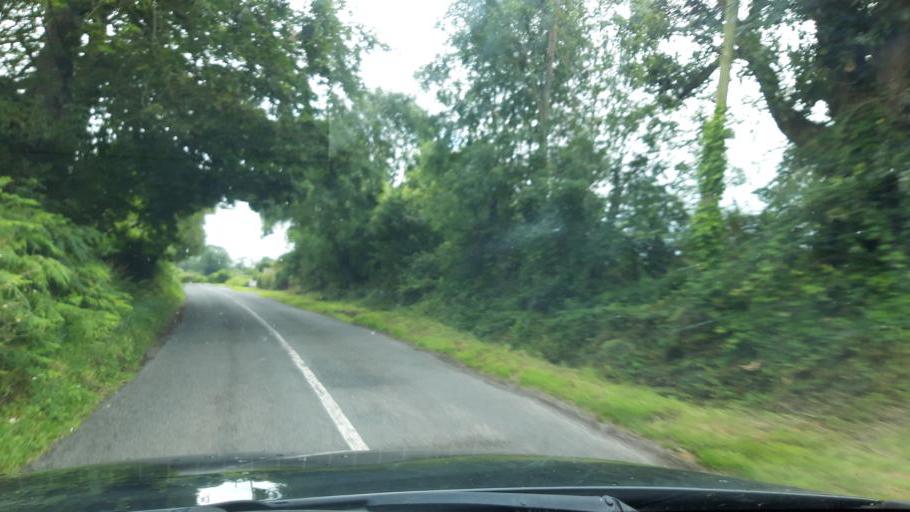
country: IE
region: Munster
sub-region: County Cork
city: Castlemartyr
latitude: 52.1354
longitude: -8.0354
